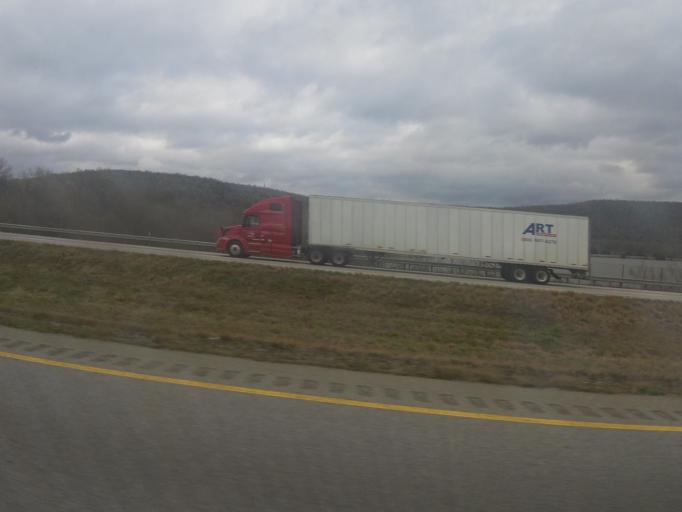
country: US
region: Tennessee
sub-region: Marion County
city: Jasper
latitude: 35.0299
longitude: -85.5740
